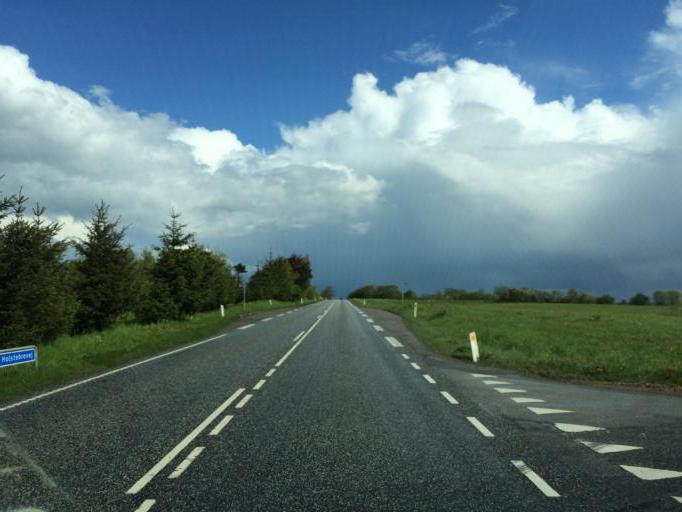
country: DK
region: Central Jutland
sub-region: Holstebro Kommune
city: Vinderup
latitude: 56.4256
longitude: 8.7087
